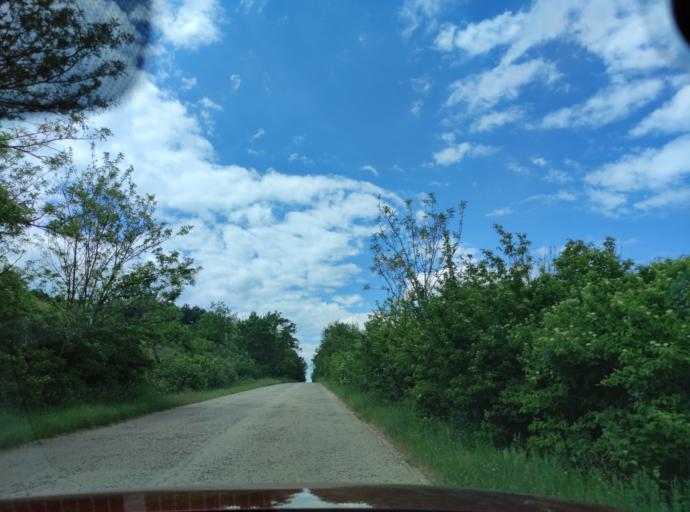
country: BG
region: Montana
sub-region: Obshtina Berkovitsa
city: Berkovitsa
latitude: 43.3578
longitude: 23.0933
